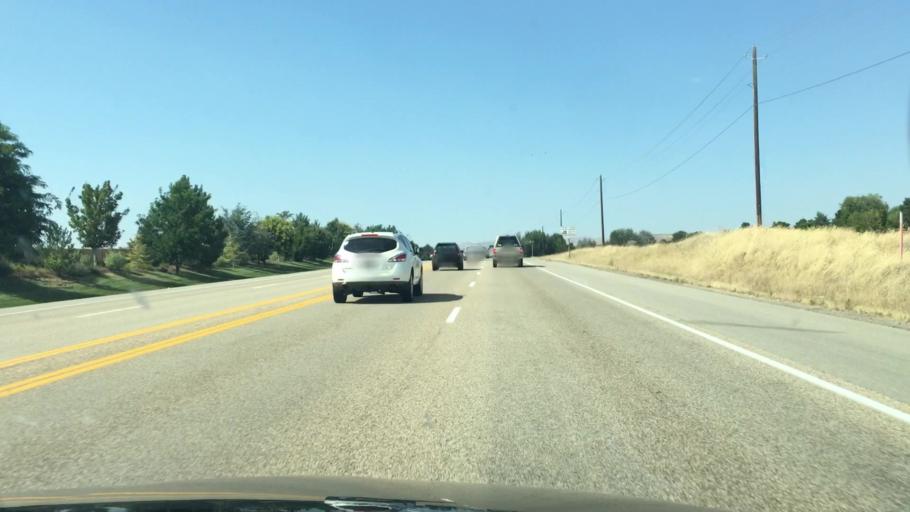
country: US
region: Idaho
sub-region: Ada County
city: Eagle
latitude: 43.6969
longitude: -116.3191
